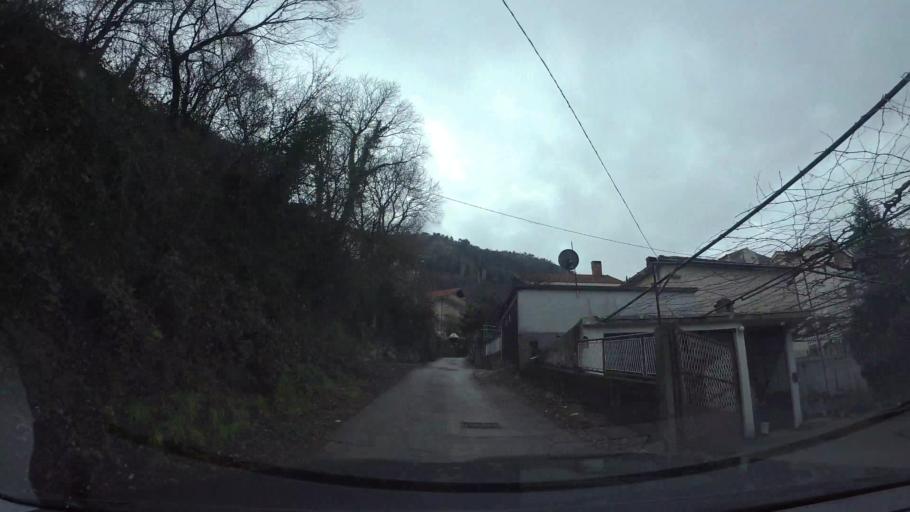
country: BA
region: Federation of Bosnia and Herzegovina
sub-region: Hercegovacko-Bosanski Kanton
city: Mostar
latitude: 43.3352
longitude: 17.8024
